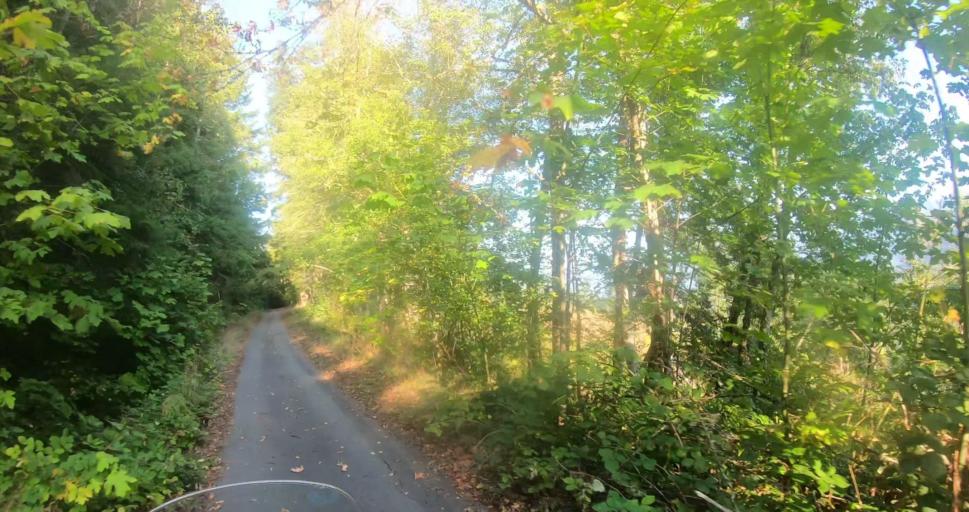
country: US
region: Washington
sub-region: Lewis County
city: Morton
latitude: 46.5428
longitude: -121.9126
